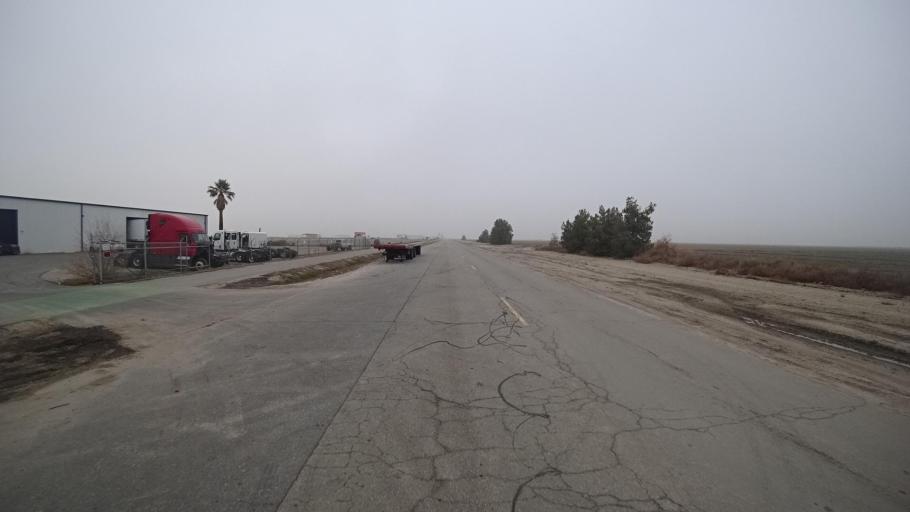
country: US
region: California
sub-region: Kern County
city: Rosedale
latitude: 35.2558
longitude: -119.2528
